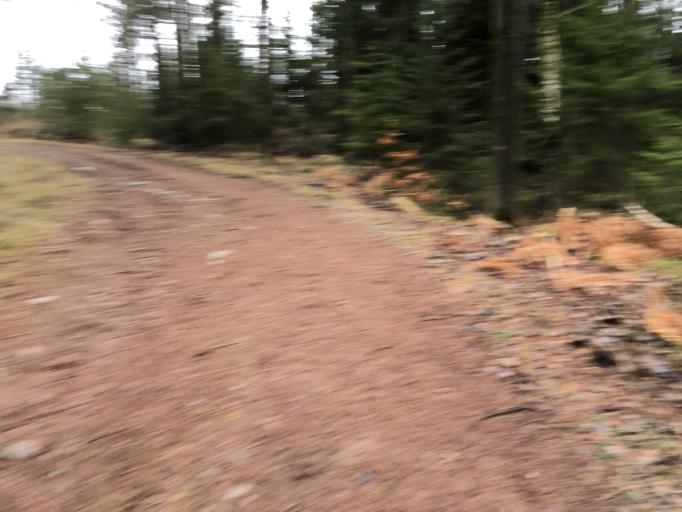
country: SE
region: Halland
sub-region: Halmstads Kommun
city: Mjallby
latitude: 56.7453
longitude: 12.8162
